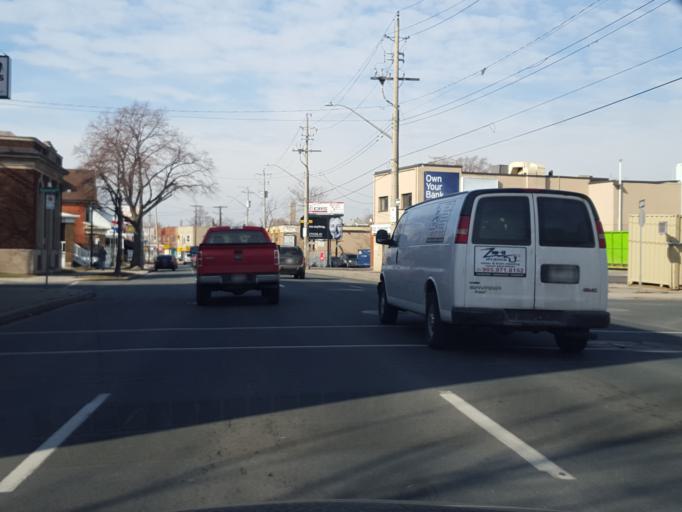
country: CA
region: Ontario
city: Hamilton
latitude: 43.2503
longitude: -79.8330
